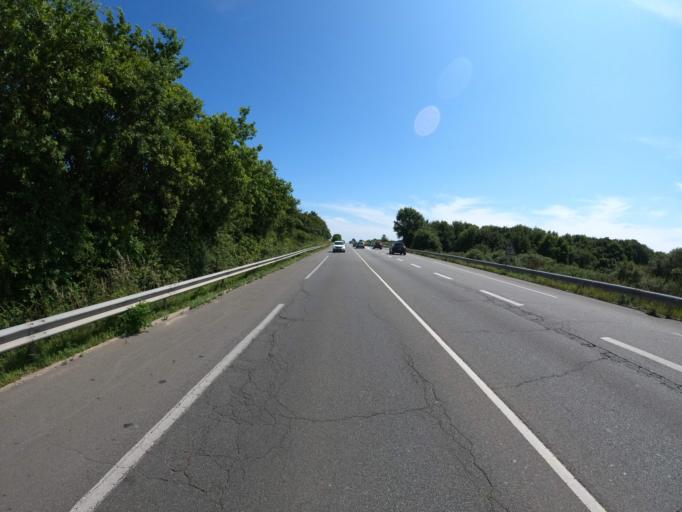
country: FR
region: Pays de la Loire
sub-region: Departement de la Loire-Atlantique
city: Saint-Nazaire
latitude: 47.2823
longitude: -2.2491
